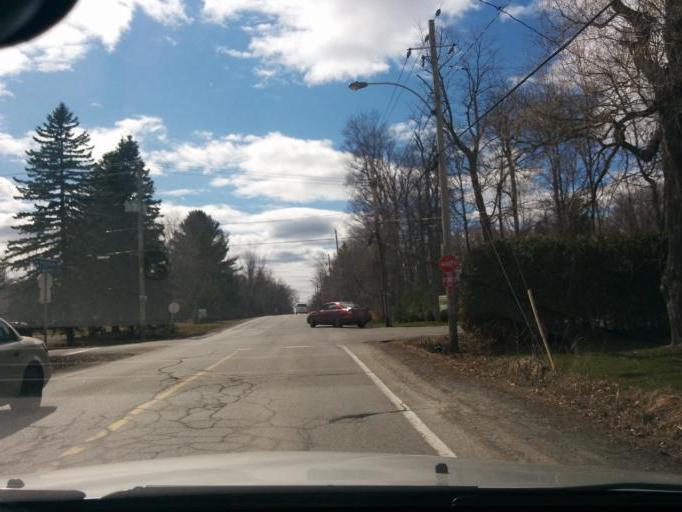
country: CA
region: Ontario
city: Ottawa
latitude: 45.4139
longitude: -75.7875
